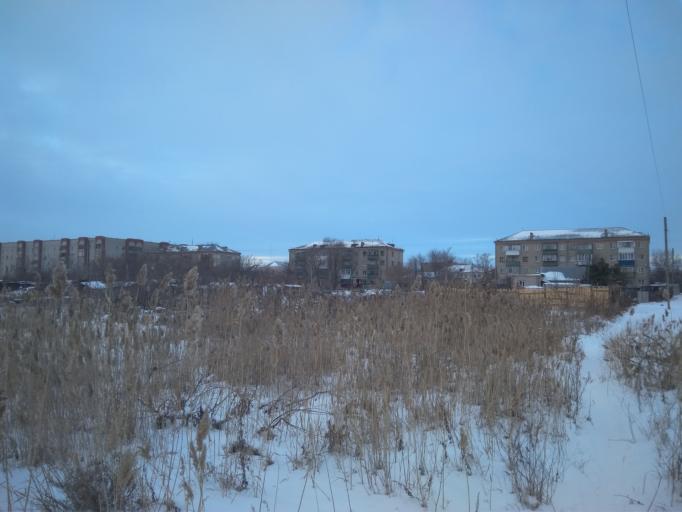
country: RU
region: Chelyabinsk
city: Troitsk
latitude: 54.0837
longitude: 61.5785
